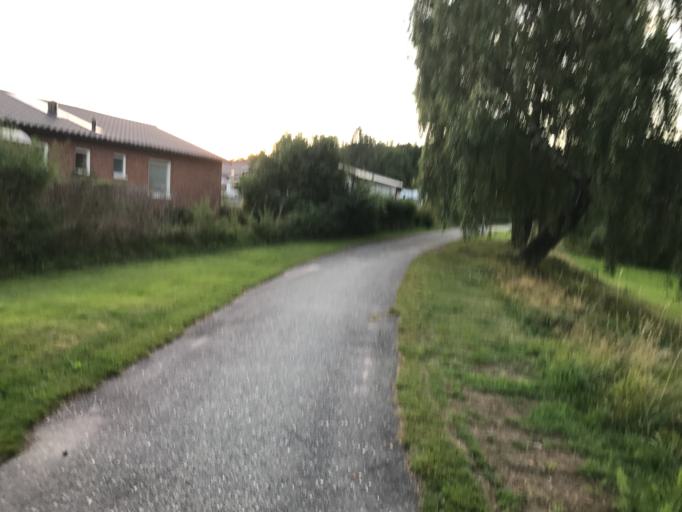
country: SE
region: Vaestra Goetaland
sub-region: Lerums Kommun
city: Lerum
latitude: 57.7789
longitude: 12.2495
